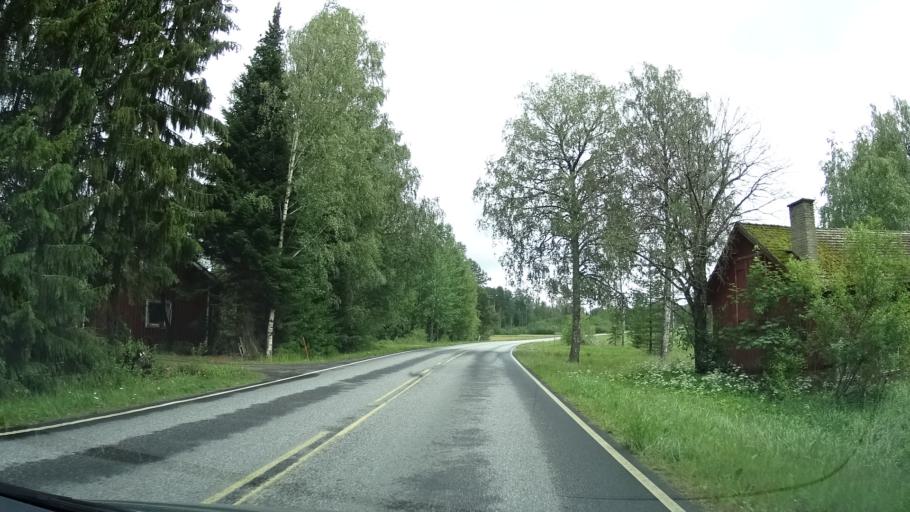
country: FI
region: Pirkanmaa
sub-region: Etelae-Pirkanmaa
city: Urjala
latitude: 61.0933
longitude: 23.3798
